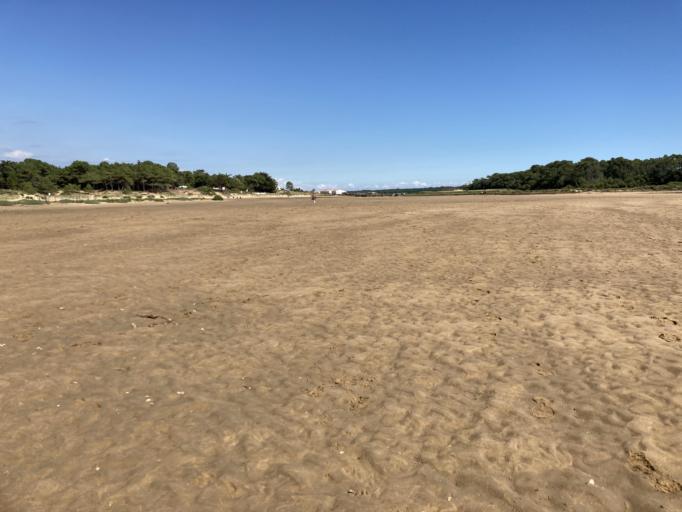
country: FR
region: Pays de la Loire
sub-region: Departement de la Vendee
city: Saint-Hilaire-de-Talmont
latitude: 46.4343
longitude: -1.6433
